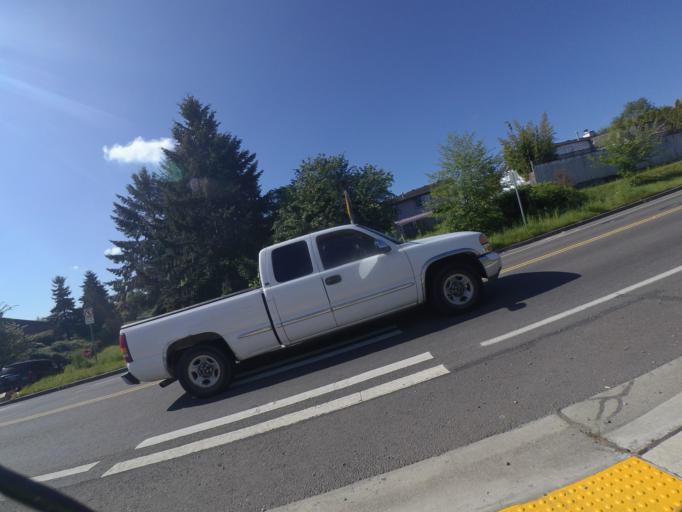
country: US
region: Washington
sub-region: Pierce County
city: Waller
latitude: 47.2136
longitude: -122.4108
